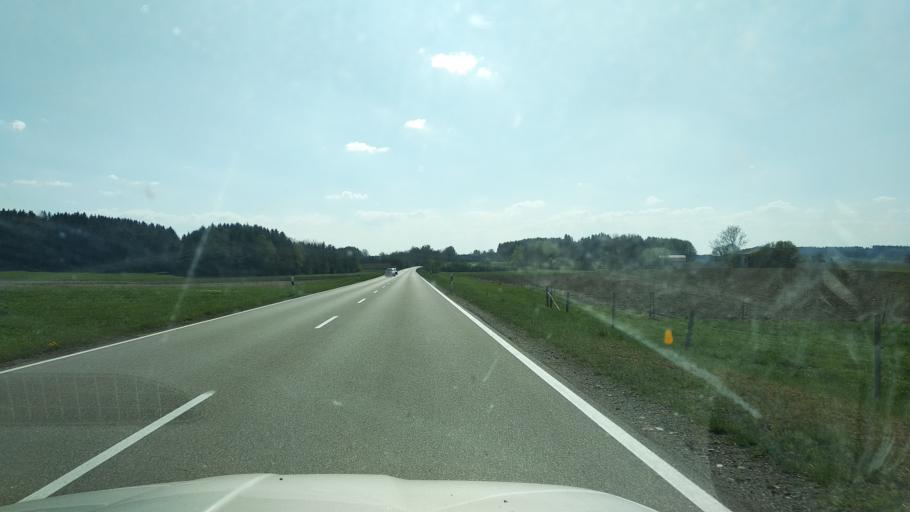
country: DE
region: Bavaria
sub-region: Swabia
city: Erkheim
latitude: 48.0414
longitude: 10.3677
